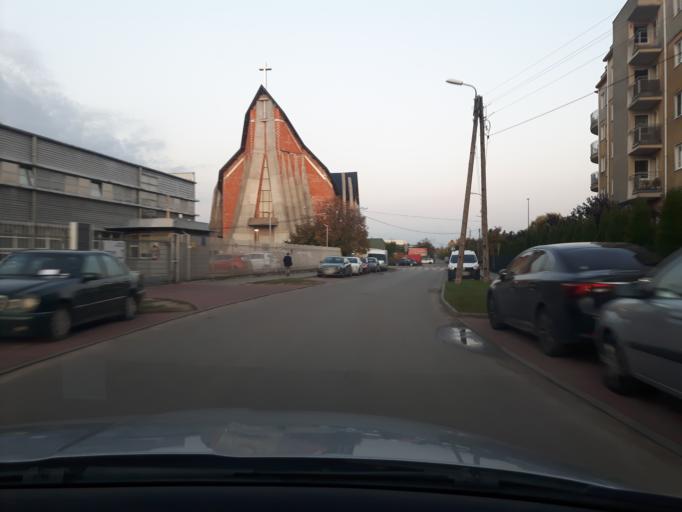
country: PL
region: Masovian Voivodeship
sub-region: Powiat wolominski
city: Zabki
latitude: 52.2852
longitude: 21.0817
